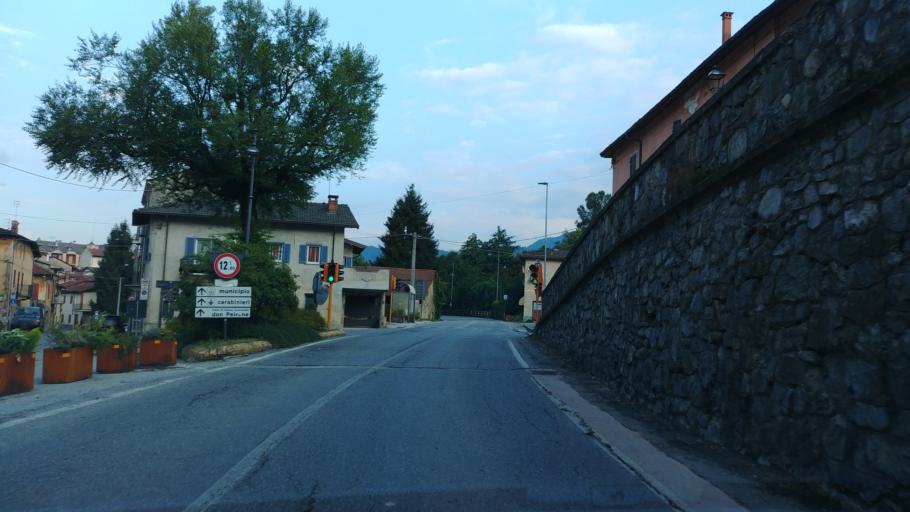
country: IT
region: Piedmont
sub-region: Provincia di Cuneo
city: Peveragno
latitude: 44.3307
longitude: 7.6112
